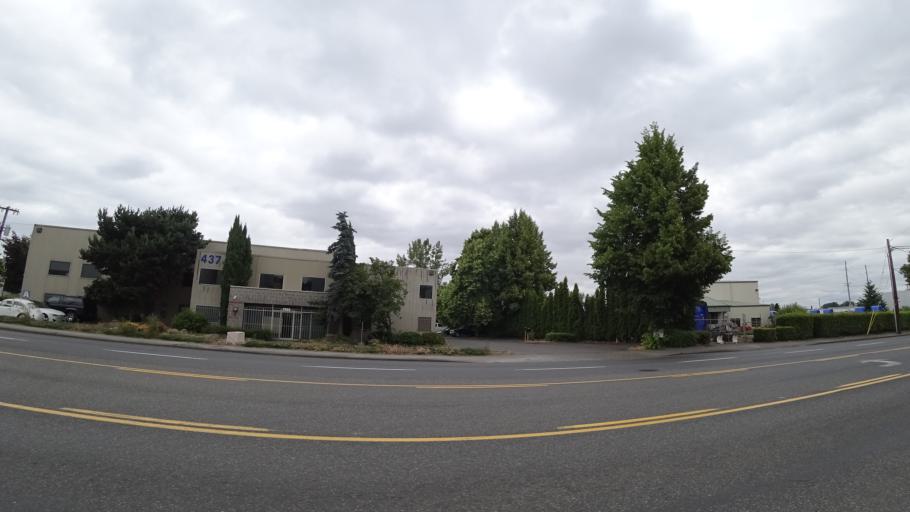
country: US
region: Washington
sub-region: Clark County
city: Vancouver
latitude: 45.5834
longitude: -122.6706
